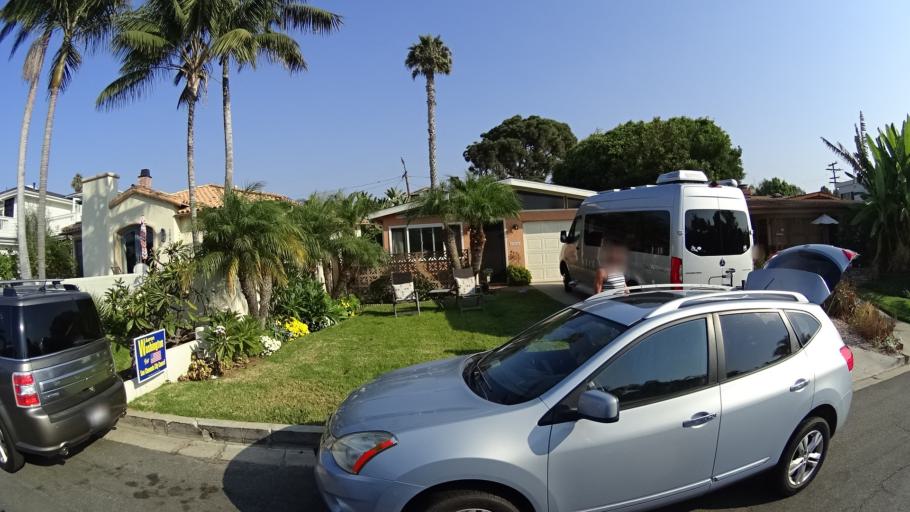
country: US
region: California
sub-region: Orange County
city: San Clemente
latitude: 33.4126
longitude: -117.6096
